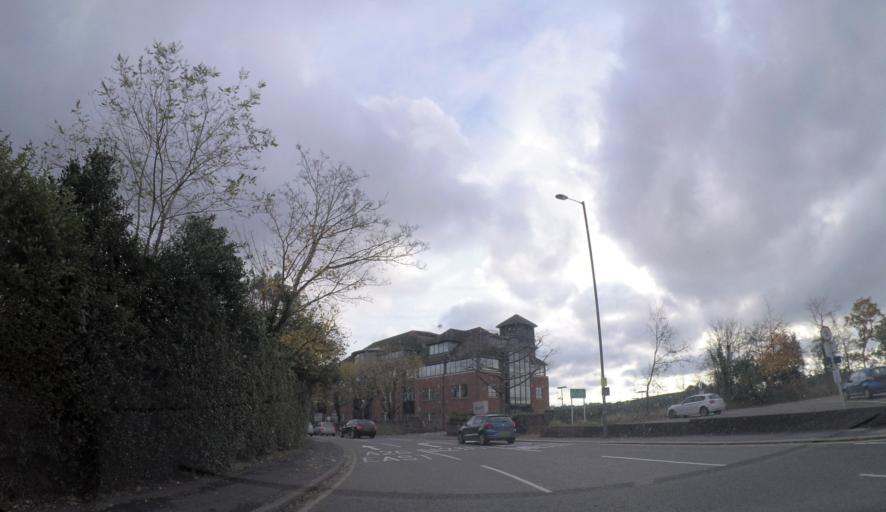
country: GB
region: England
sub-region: Surrey
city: Reigate
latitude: 51.2390
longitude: -0.2046
